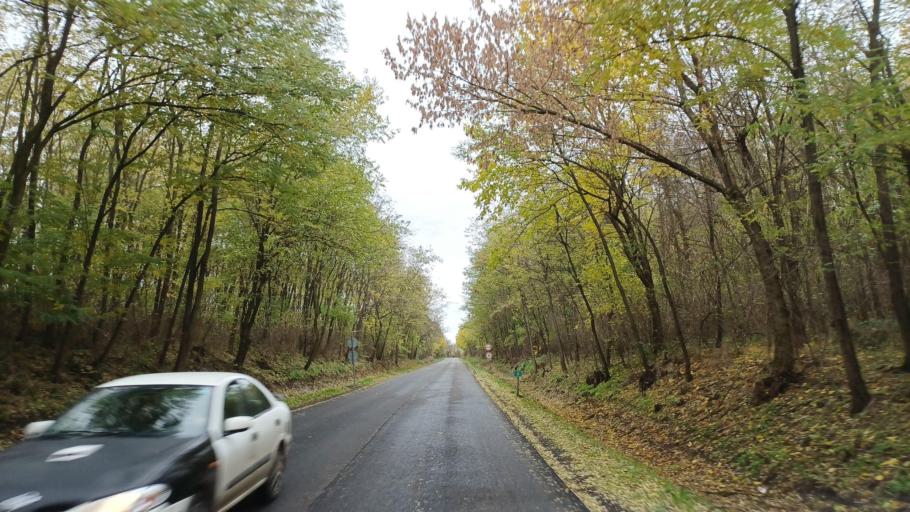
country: HU
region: Tolna
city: Tengelic
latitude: 46.5336
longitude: 18.7608
